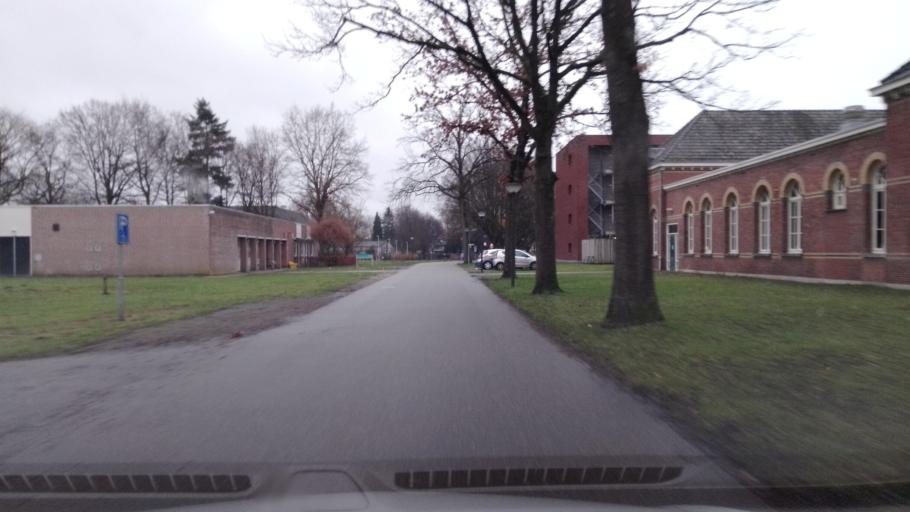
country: NL
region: Limburg
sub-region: Gemeente Venray
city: Venray
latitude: 51.5263
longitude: 5.9897
